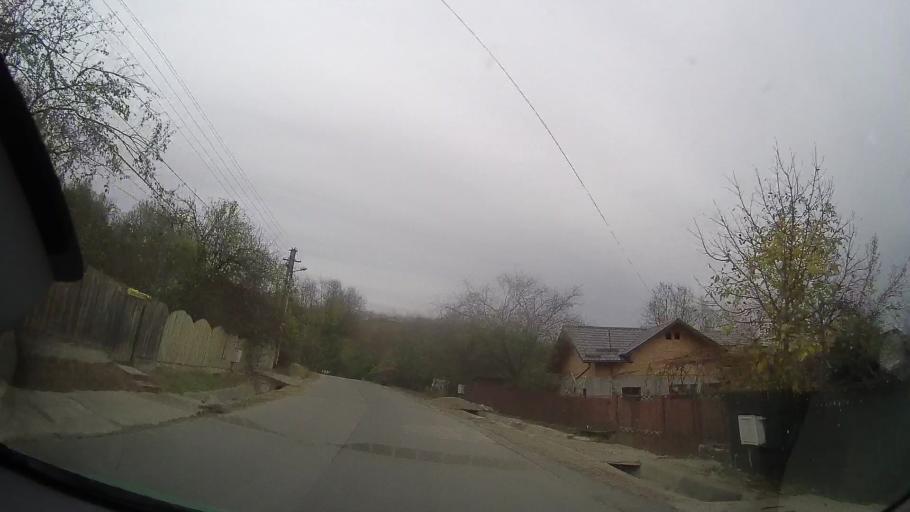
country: RO
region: Prahova
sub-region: Comuna Gornet-Cricov
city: Gornet-Cricov
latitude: 45.0581
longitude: 26.2824
